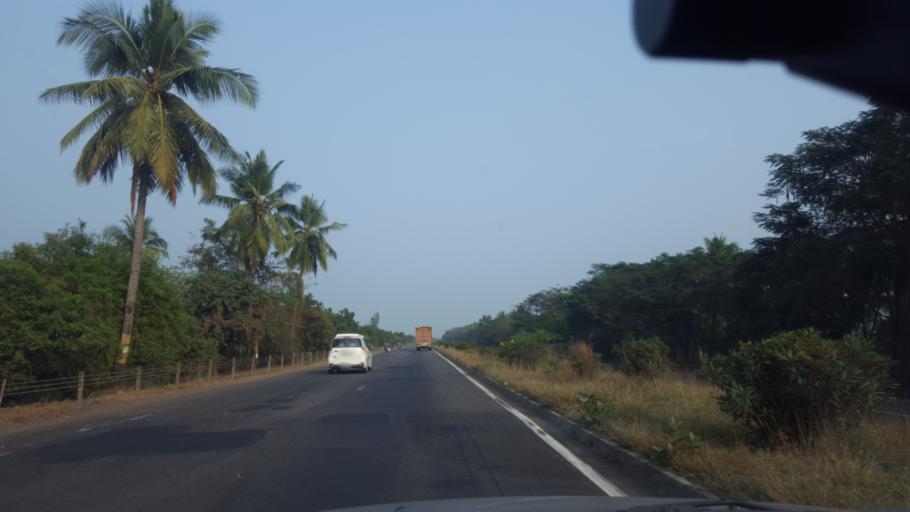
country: IN
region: Andhra Pradesh
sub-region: West Godavari
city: Tadepallegudem
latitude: 16.8242
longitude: 81.4475
